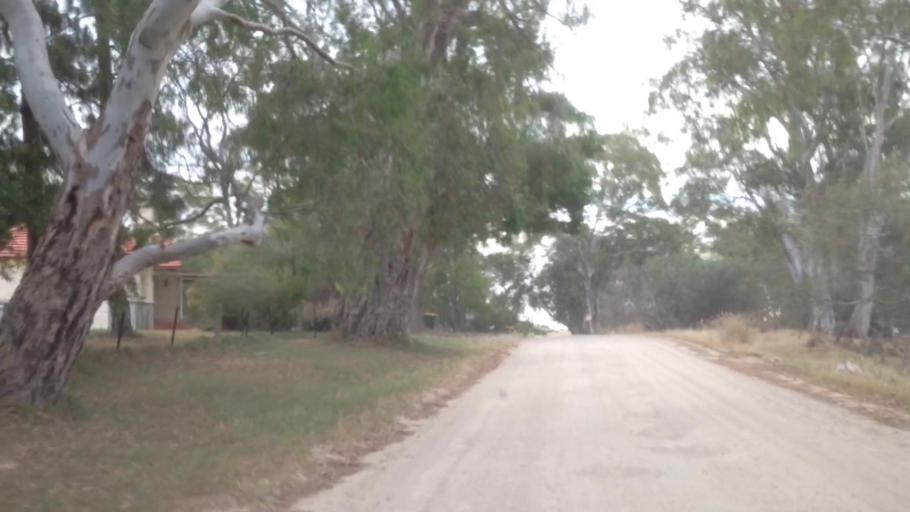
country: AU
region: South Australia
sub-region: Barossa
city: Lyndoch
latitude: -34.5989
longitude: 138.9321
